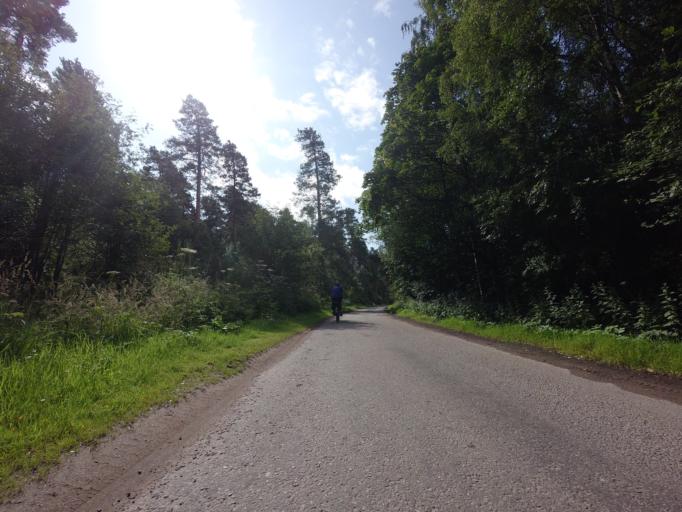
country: GB
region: Scotland
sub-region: Highland
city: Nairn
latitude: 57.5586
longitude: -3.8664
